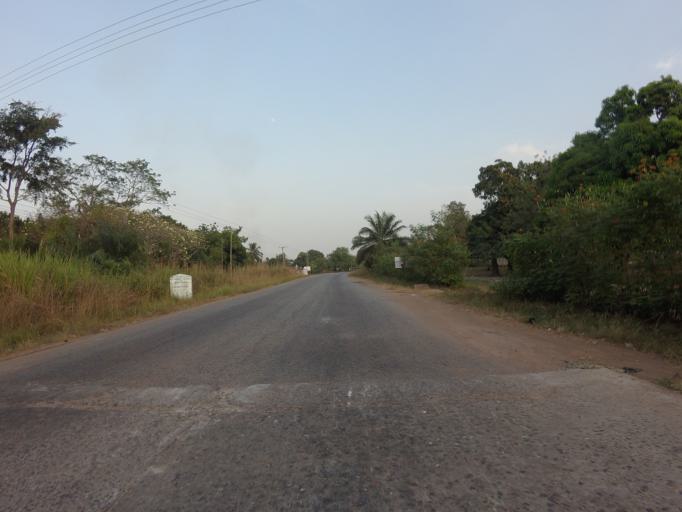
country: GH
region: Volta
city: Ho
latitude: 6.5731
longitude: 0.3834
